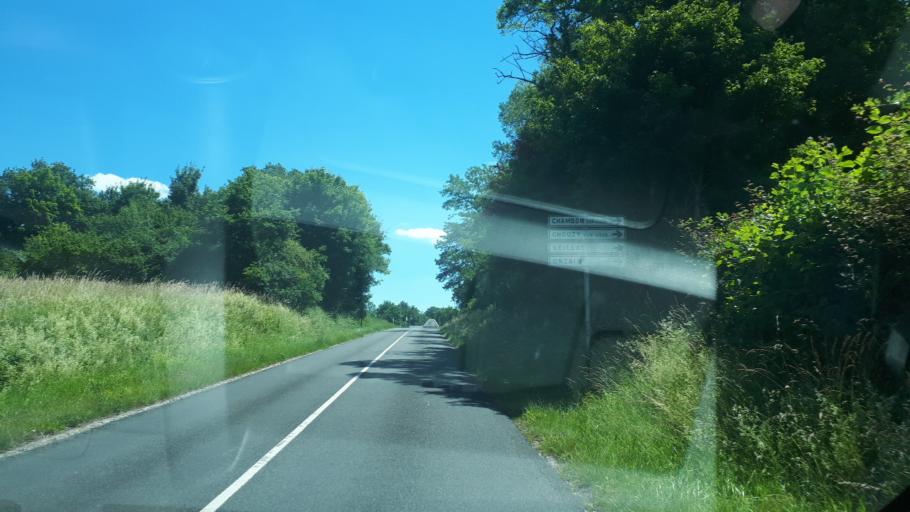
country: FR
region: Centre
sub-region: Departement du Loir-et-Cher
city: Chouzy-sur-Cisse
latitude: 47.5663
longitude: 1.2160
